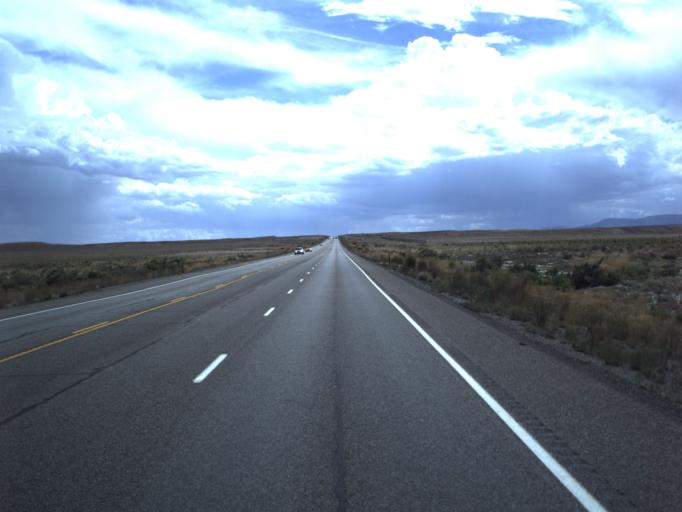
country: US
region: Utah
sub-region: Carbon County
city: Price
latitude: 39.5121
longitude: -110.8323
